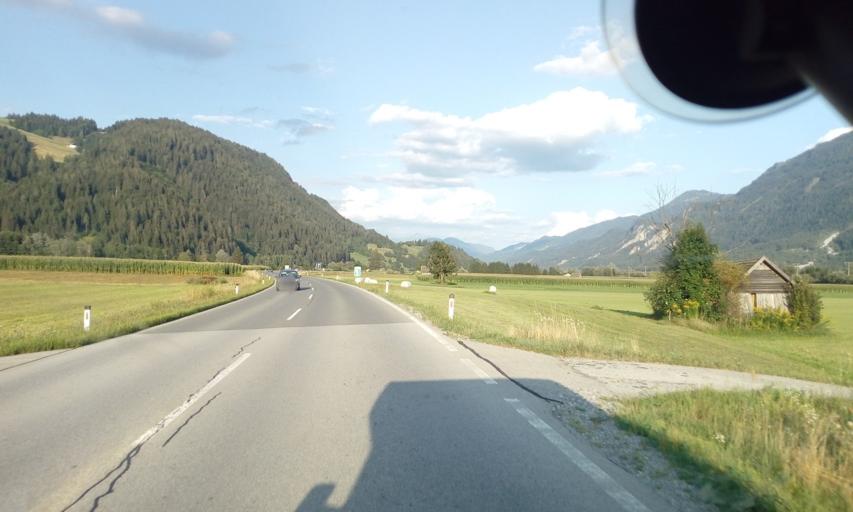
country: AT
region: Carinthia
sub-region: Politischer Bezirk Spittal an der Drau
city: Irschen
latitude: 46.7407
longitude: 13.0362
